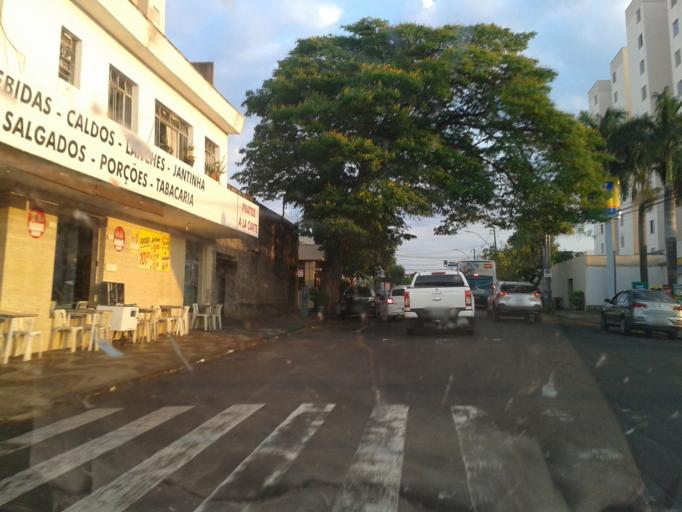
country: BR
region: Minas Gerais
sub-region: Uberlandia
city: Uberlandia
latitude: -18.9068
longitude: -48.2785
